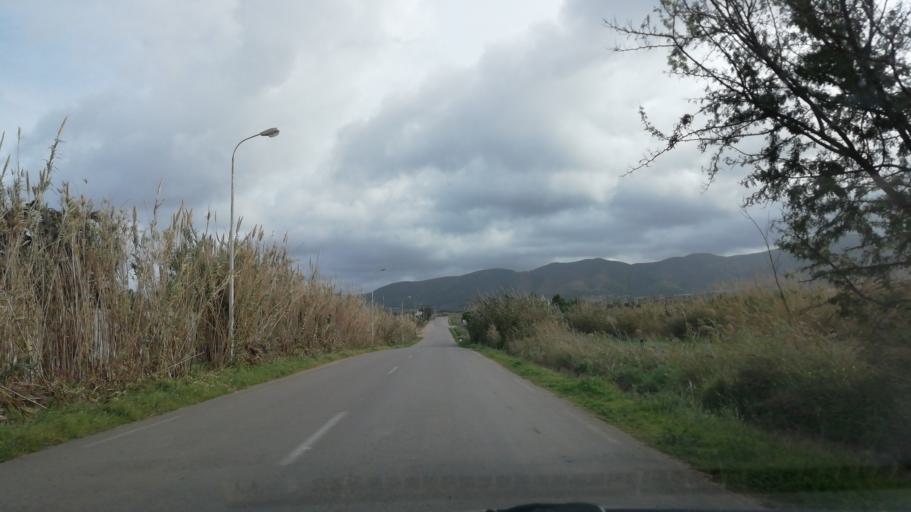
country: DZ
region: Oran
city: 'Ain el Turk
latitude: 35.7007
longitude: -0.8877
